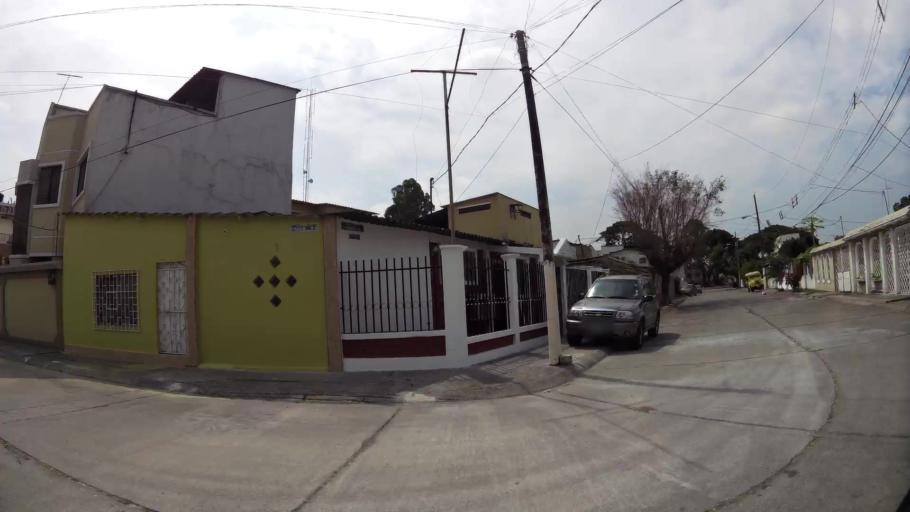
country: EC
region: Guayas
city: Eloy Alfaro
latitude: -2.1208
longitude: -79.8944
